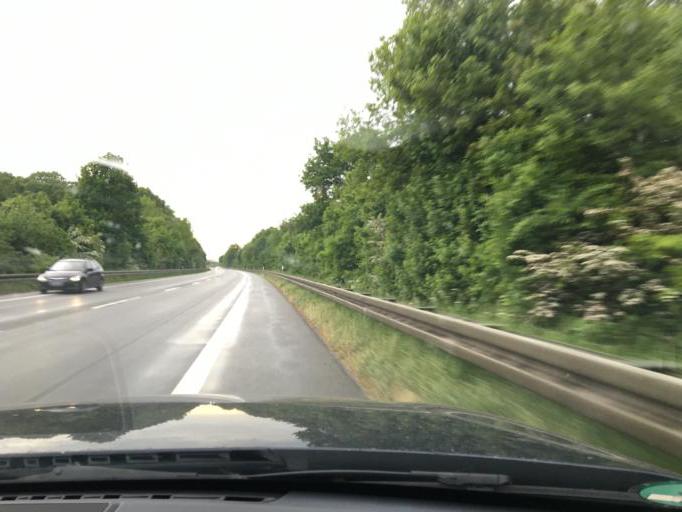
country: DE
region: North Rhine-Westphalia
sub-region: Regierungsbezirk Munster
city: Greven
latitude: 52.1233
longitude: 7.5923
